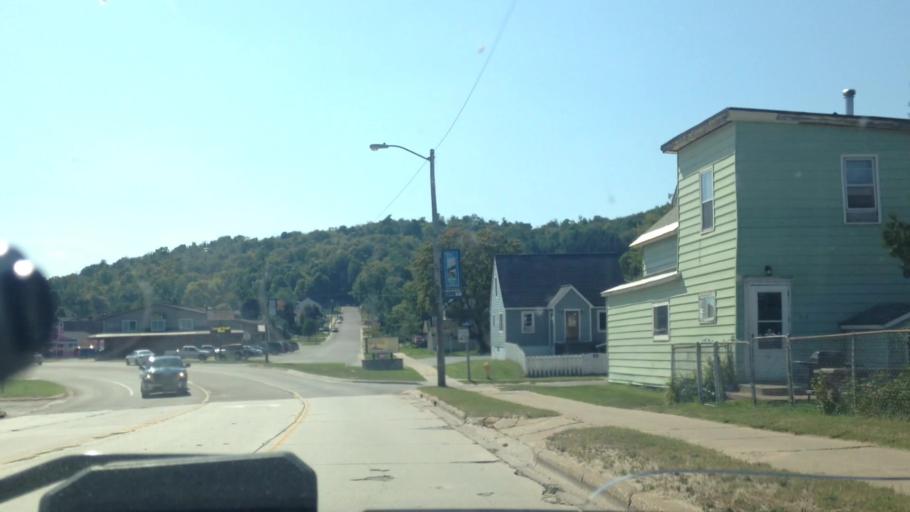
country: US
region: Michigan
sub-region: Alger County
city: Munising
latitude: 46.4084
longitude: -86.6509
